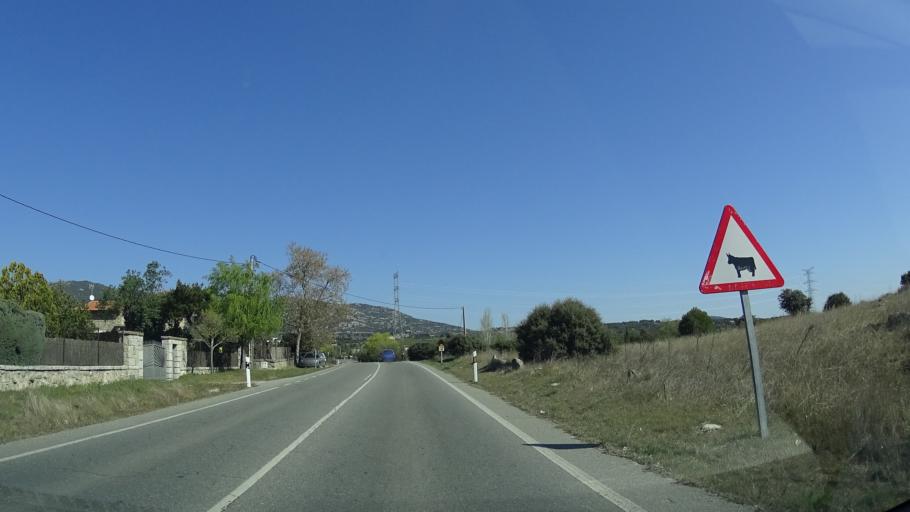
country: ES
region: Madrid
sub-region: Provincia de Madrid
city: Hoyo de Manzanares
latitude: 40.6088
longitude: -3.9038
